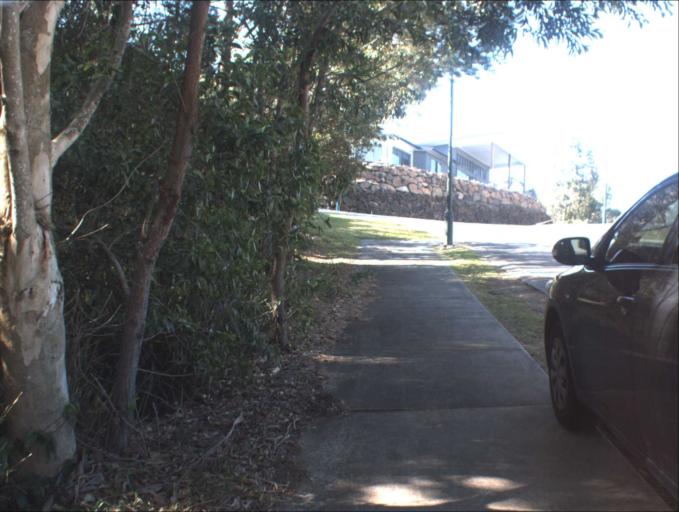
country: AU
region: Queensland
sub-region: Logan
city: Slacks Creek
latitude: -27.6301
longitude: 153.1577
